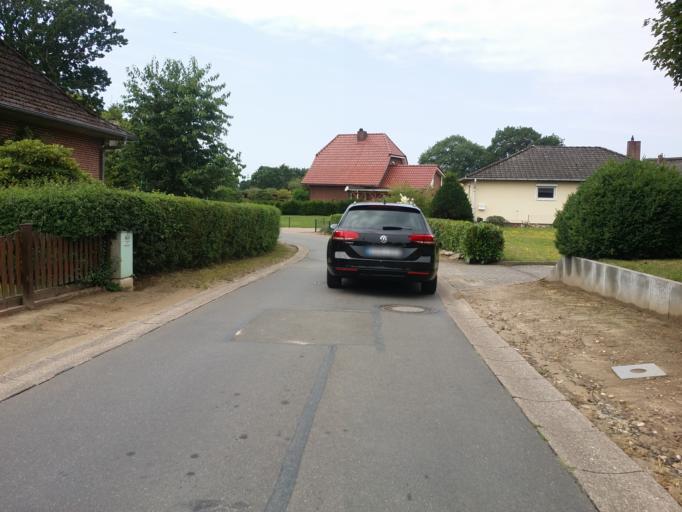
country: DE
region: Schleswig-Holstein
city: Oldendorf
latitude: 53.9567
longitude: 9.4535
